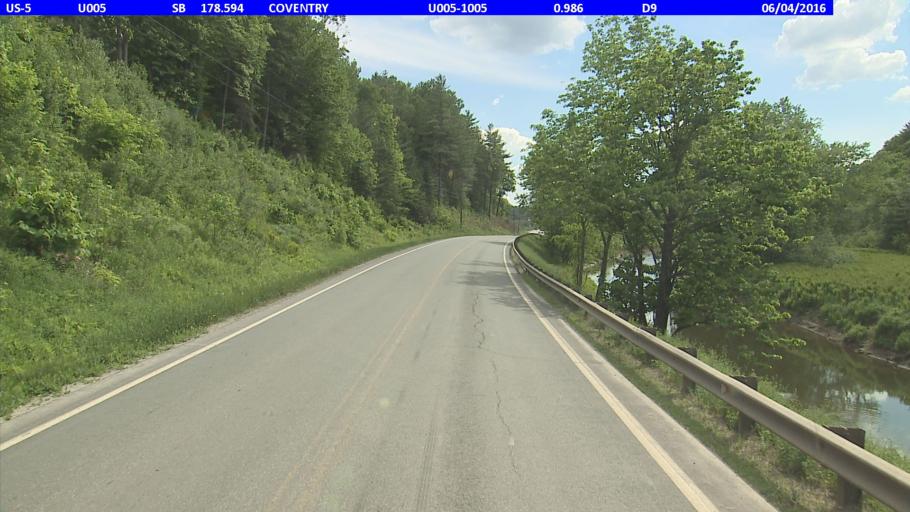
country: US
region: Vermont
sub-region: Orleans County
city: Newport
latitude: 44.8713
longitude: -72.2569
